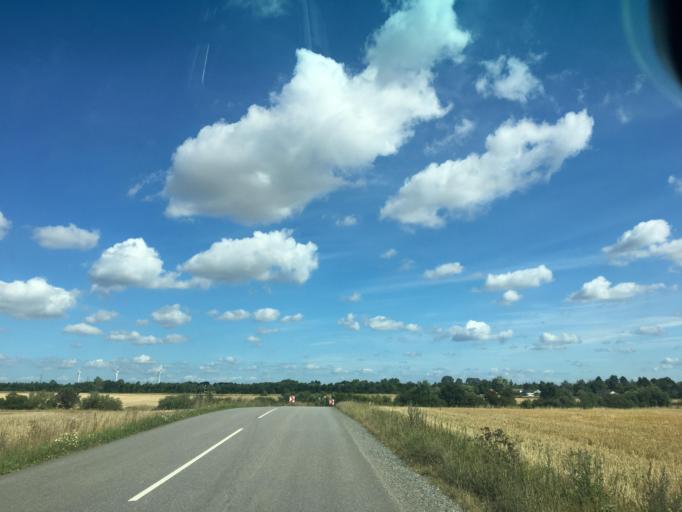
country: DK
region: Zealand
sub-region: Solrod Kommune
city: Solrod Strand
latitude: 55.5696
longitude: 12.2130
